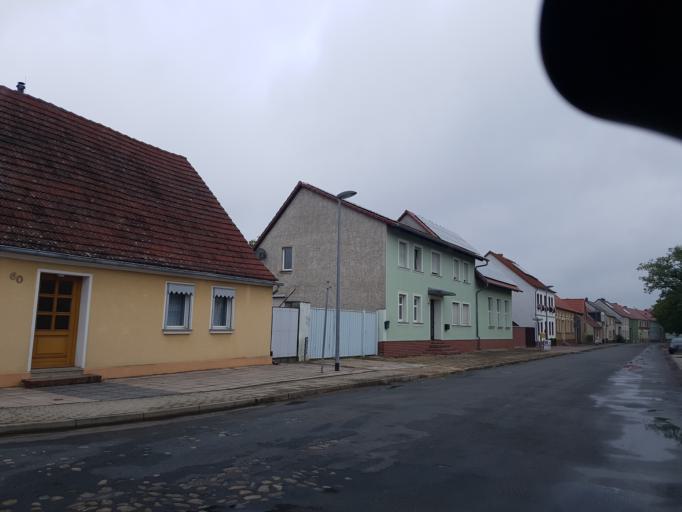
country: DE
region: Brandenburg
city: Gorzke
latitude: 52.1384
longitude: 12.3107
